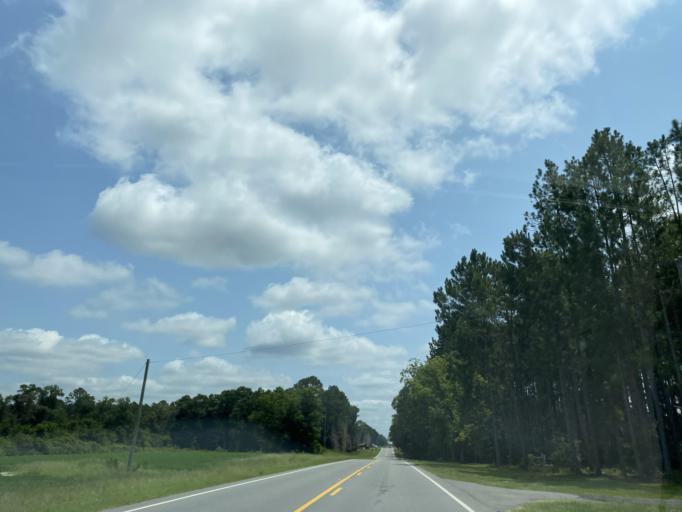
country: US
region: Georgia
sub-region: Jeff Davis County
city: Hazlehurst
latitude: 31.7158
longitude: -82.5222
